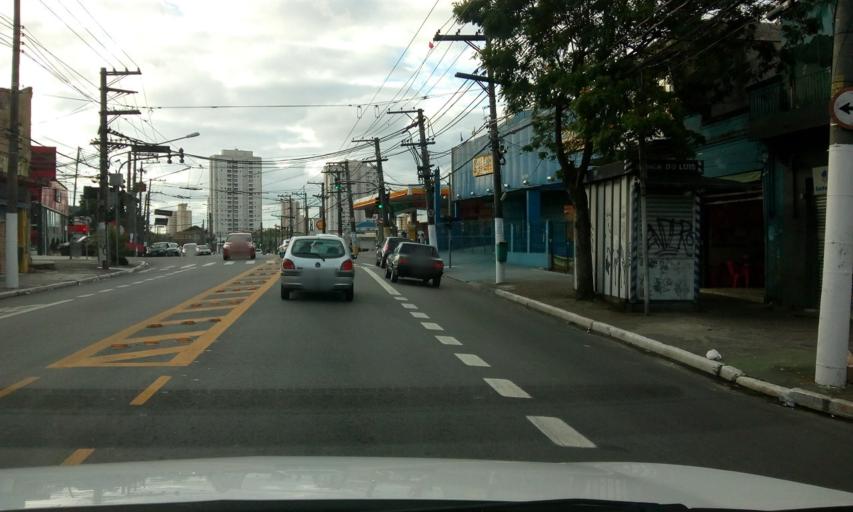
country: BR
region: Sao Paulo
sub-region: Sao Caetano Do Sul
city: Sao Caetano do Sul
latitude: -23.5594
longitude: -46.5204
